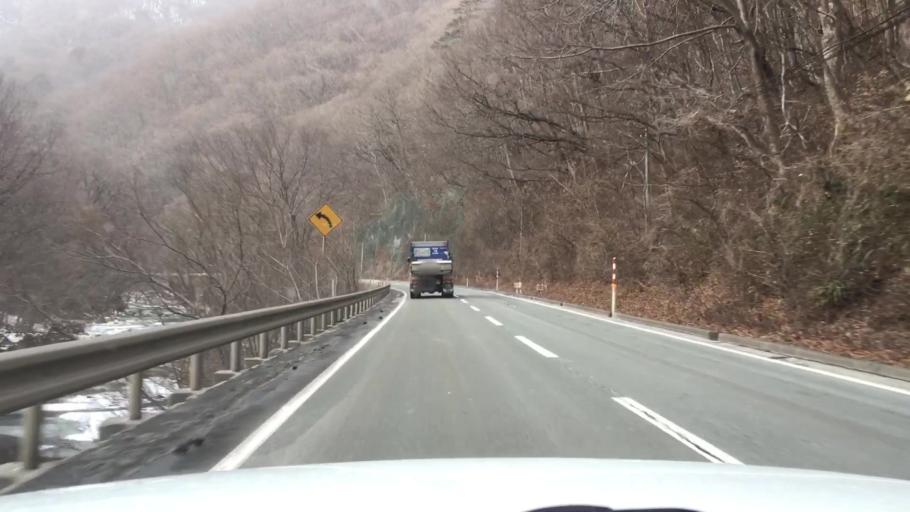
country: JP
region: Iwate
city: Tono
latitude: 39.6184
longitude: 141.4966
